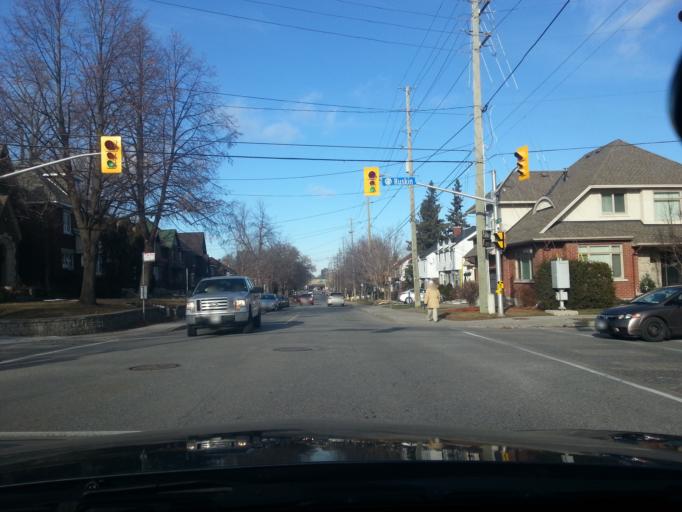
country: CA
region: Ontario
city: Ottawa
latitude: 45.3933
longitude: -75.7246
